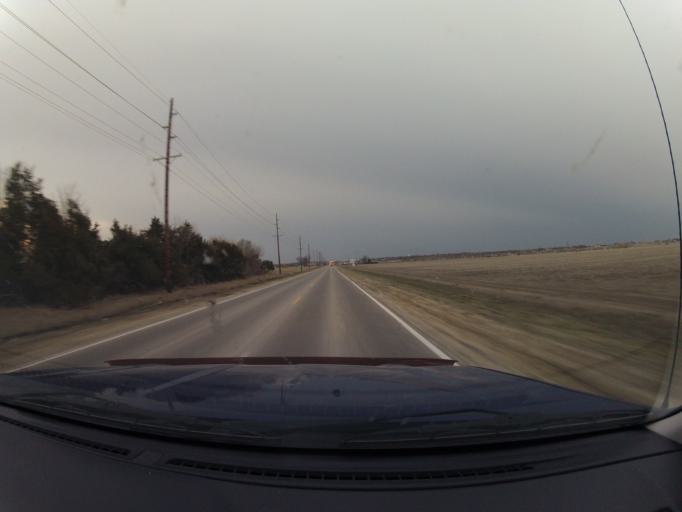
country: US
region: Nebraska
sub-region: Buffalo County
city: Kearney
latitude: 40.7138
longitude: -99.0471
